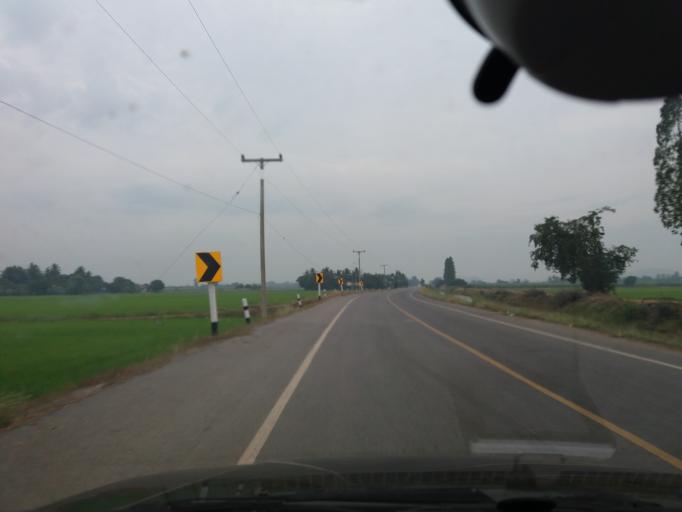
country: TH
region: Suphan Buri
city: Doem Bang Nang Buat
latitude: 14.8730
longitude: 100.1335
